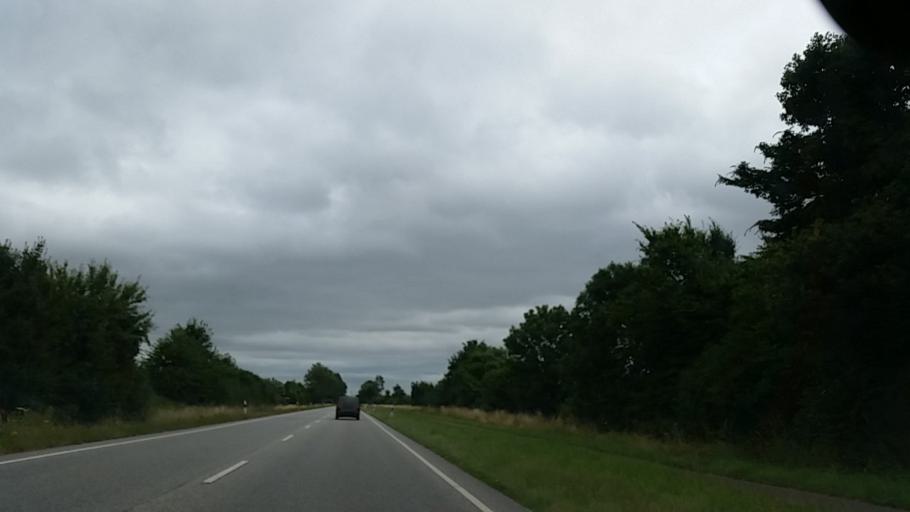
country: DE
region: Schleswig-Holstein
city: Neudorf-Bornstein
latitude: 54.4299
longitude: 9.9488
